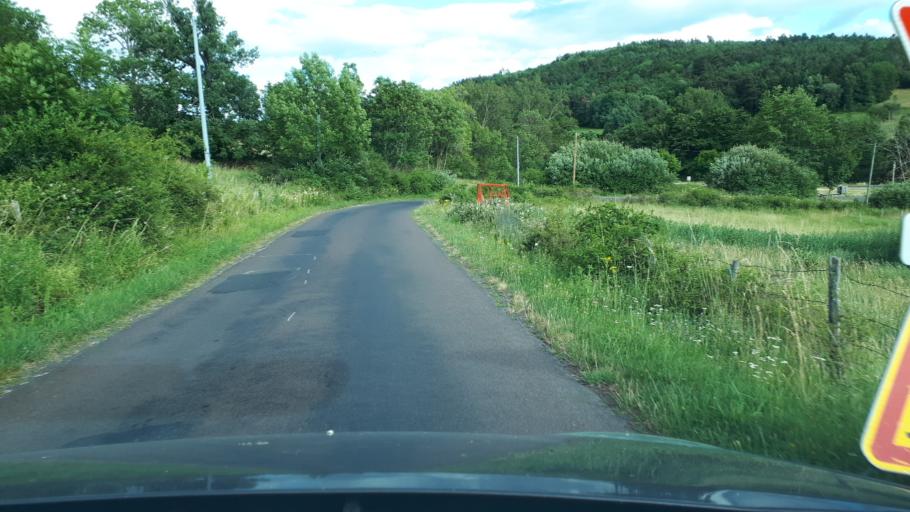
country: FR
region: Auvergne
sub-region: Departement du Puy-de-Dome
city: Aydat
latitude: 45.5906
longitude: 2.9631
